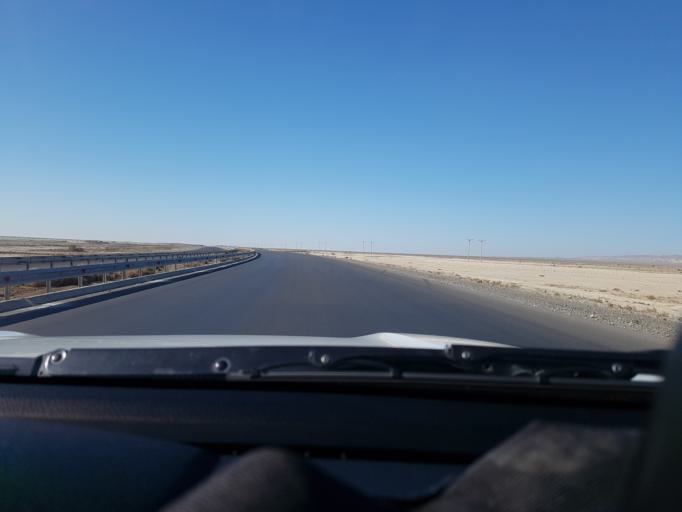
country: TM
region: Balkan
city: Gazanjyk
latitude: 39.2632
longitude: 55.1169
